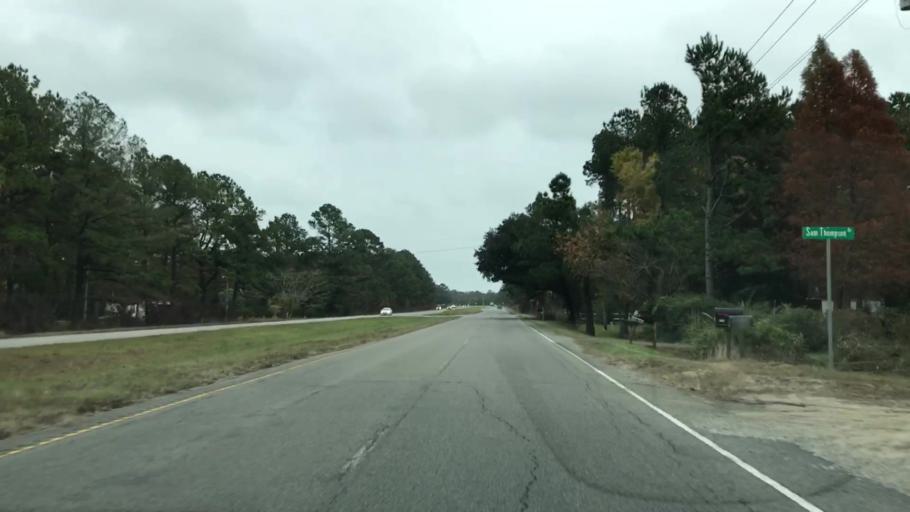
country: US
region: South Carolina
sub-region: Charleston County
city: Awendaw
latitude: 33.0383
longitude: -79.6041
